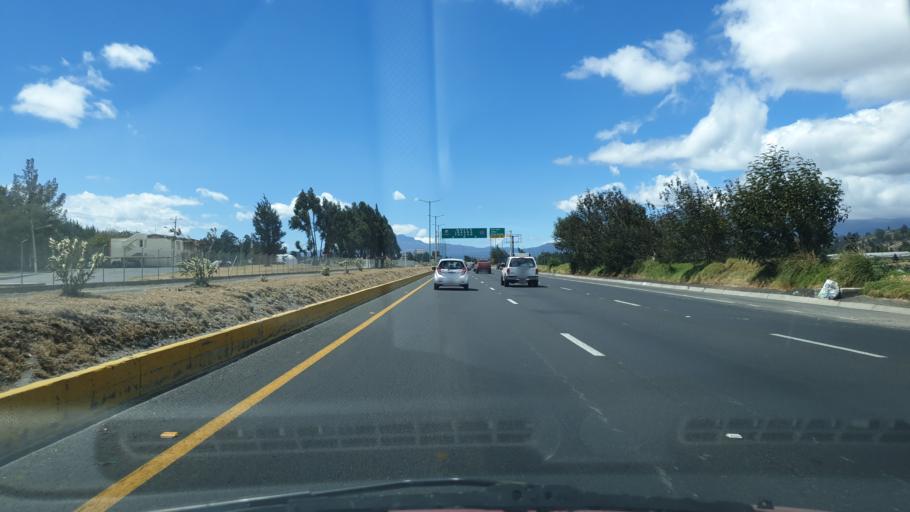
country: EC
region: Cotopaxi
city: Saquisili
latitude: -0.8574
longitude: -78.6219
